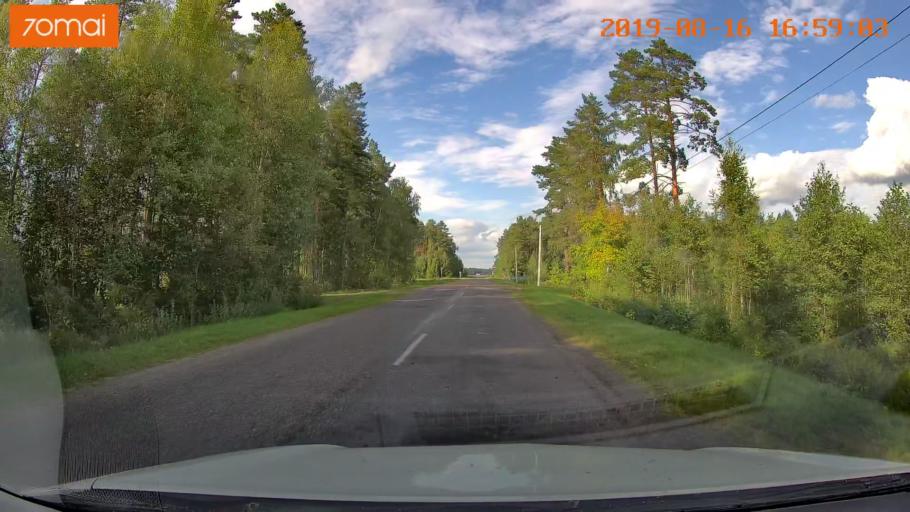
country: BY
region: Mogilev
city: Hlusha
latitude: 53.2775
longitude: 28.8388
